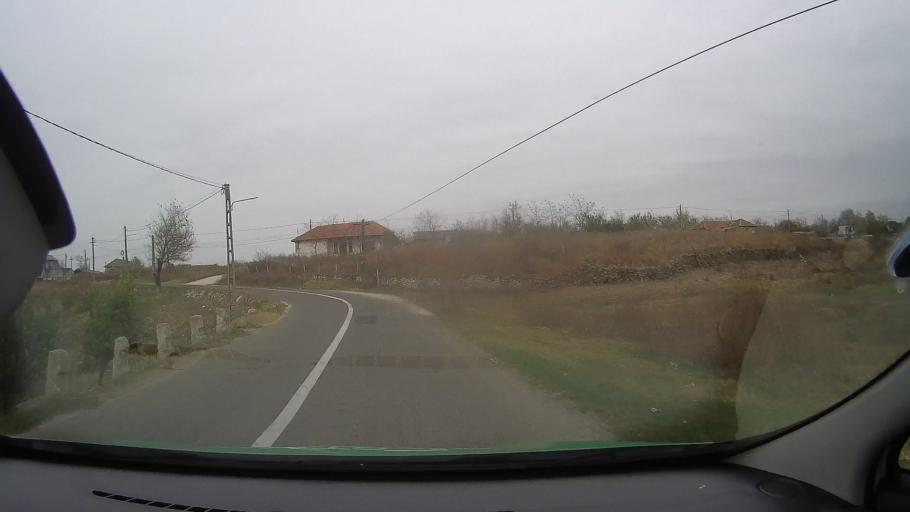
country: RO
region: Constanta
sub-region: Comuna Vulturu
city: Vulturu
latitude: 44.7007
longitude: 28.2404
